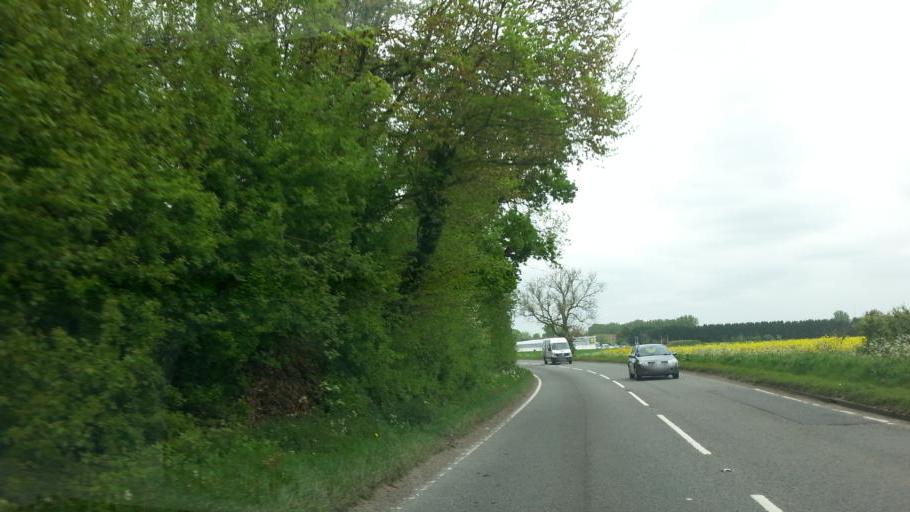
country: GB
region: England
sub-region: Lincolnshire
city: Bourne
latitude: 52.7509
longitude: -0.3702
